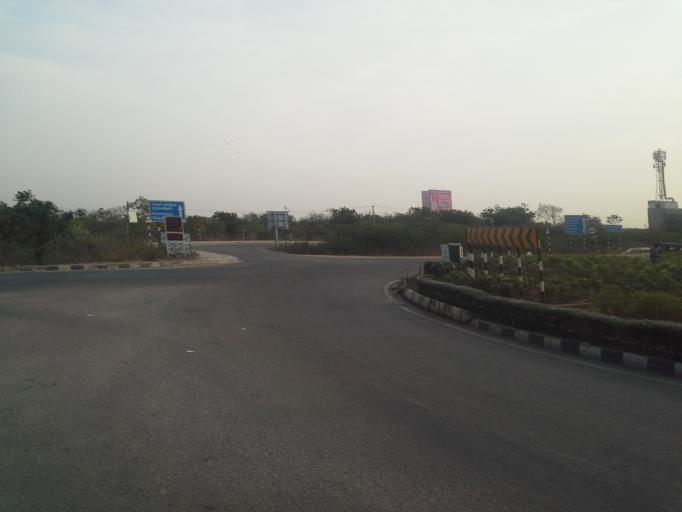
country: IN
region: Telangana
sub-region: Hyderabad
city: Hyderabad
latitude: 17.3505
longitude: 78.3622
